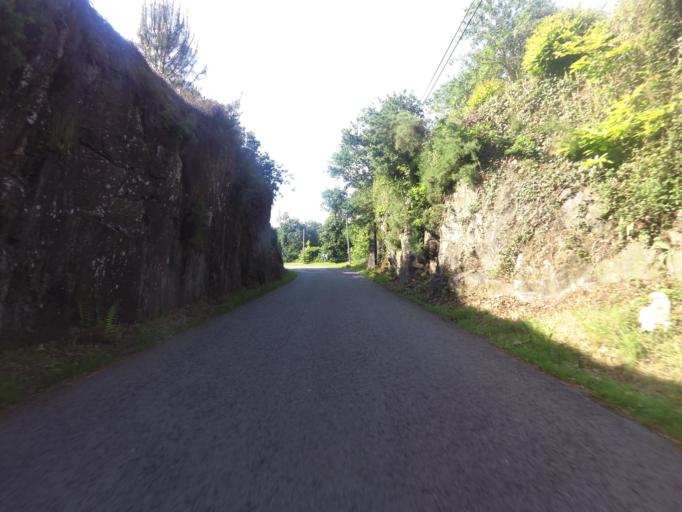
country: FR
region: Brittany
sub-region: Departement du Morbihan
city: Pluherlin
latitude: 47.7072
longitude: -2.3691
